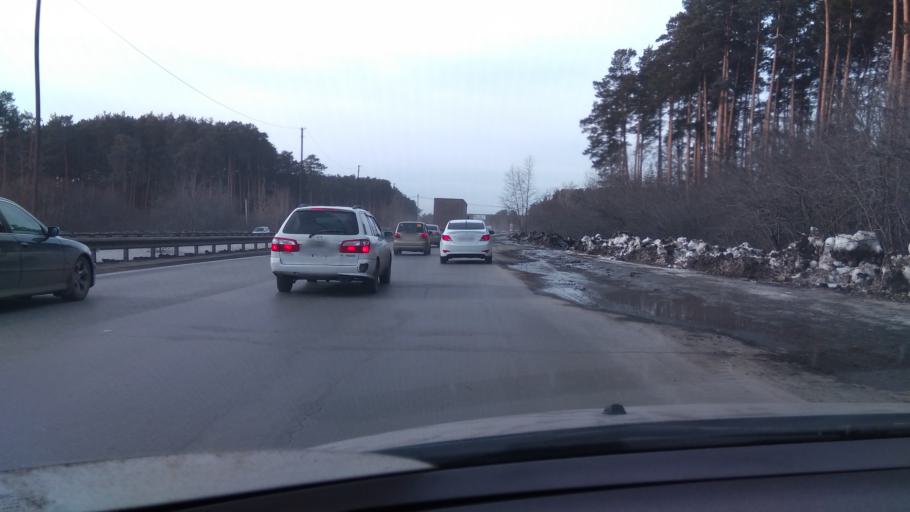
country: RU
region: Sverdlovsk
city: Shirokaya Rechka
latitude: 56.8145
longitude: 60.5149
